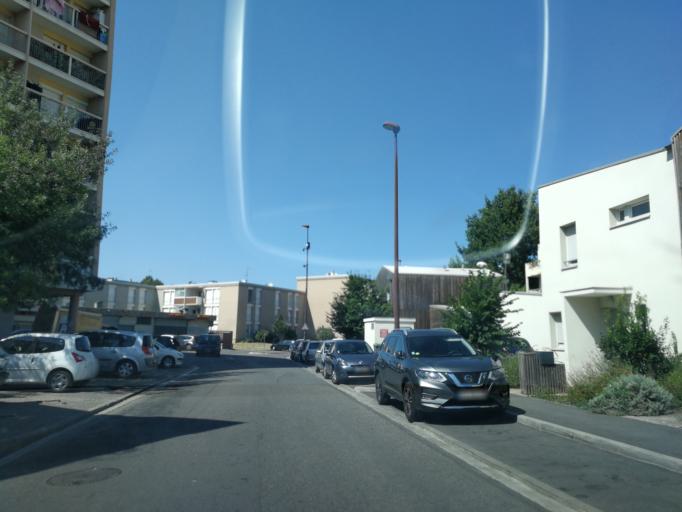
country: FR
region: Midi-Pyrenees
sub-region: Departement de la Haute-Garonne
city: L'Union
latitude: 43.6284
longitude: 1.4693
